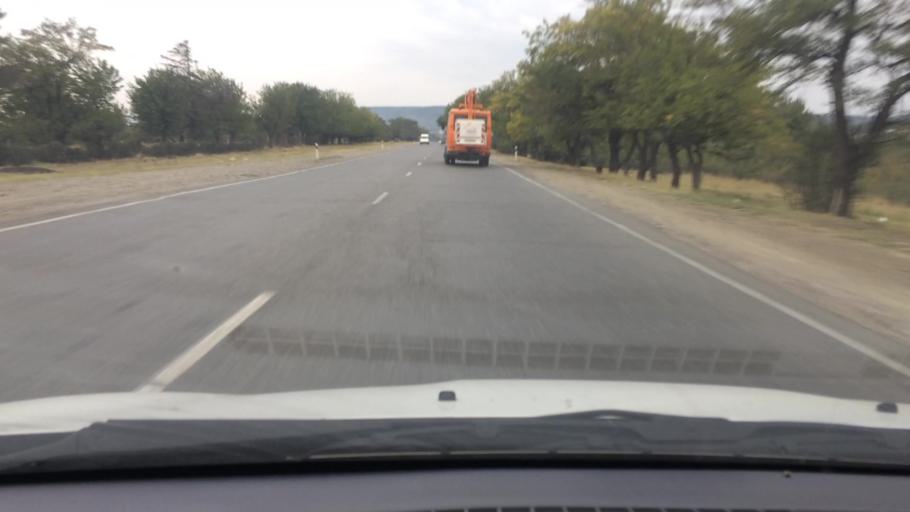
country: GE
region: T'bilisi
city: Tbilisi
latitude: 41.6412
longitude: 44.8627
